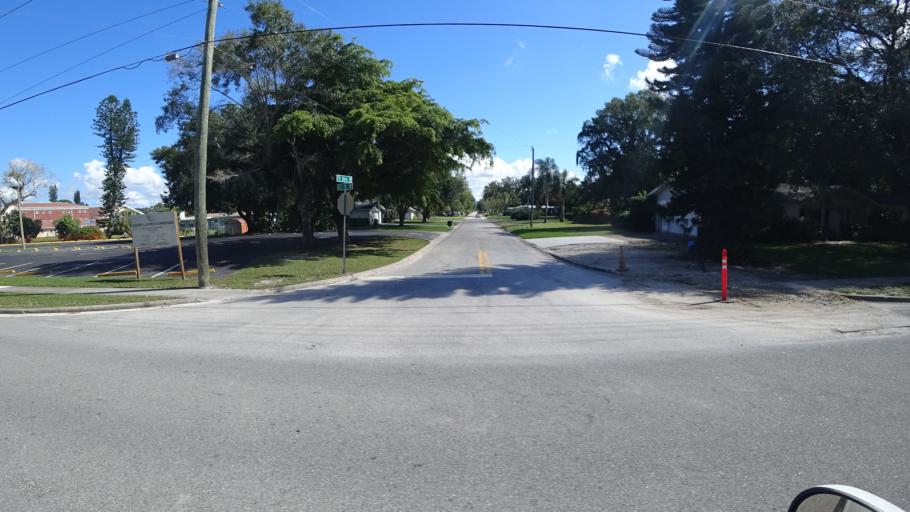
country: US
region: Florida
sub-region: Manatee County
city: West Bradenton
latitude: 27.4867
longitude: -82.6040
